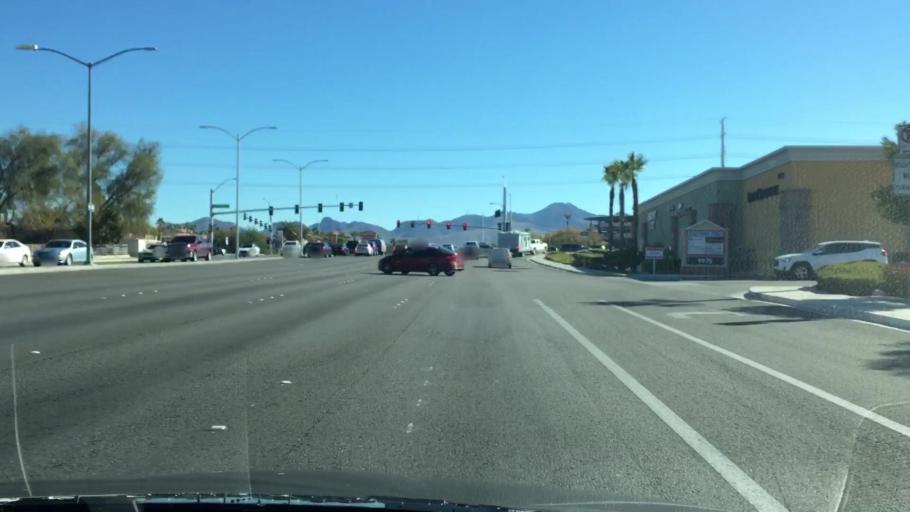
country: US
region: Nevada
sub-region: Clark County
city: Whitney
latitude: 36.0081
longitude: -115.1155
